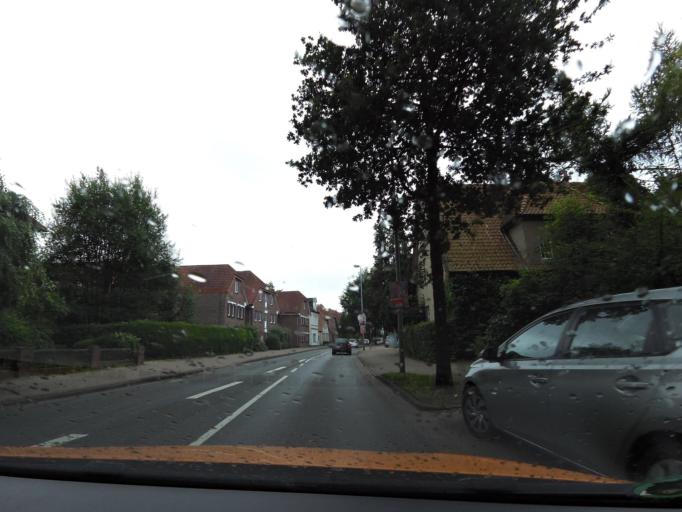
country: DE
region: Lower Saxony
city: Oldenburg
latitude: 53.1278
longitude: 8.2213
